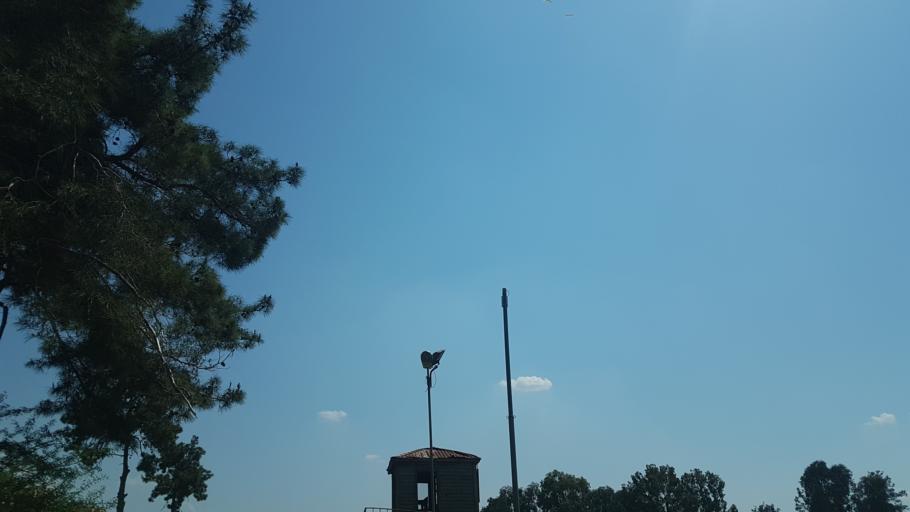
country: TR
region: Adana
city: Adana
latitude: 37.0299
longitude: 35.3542
